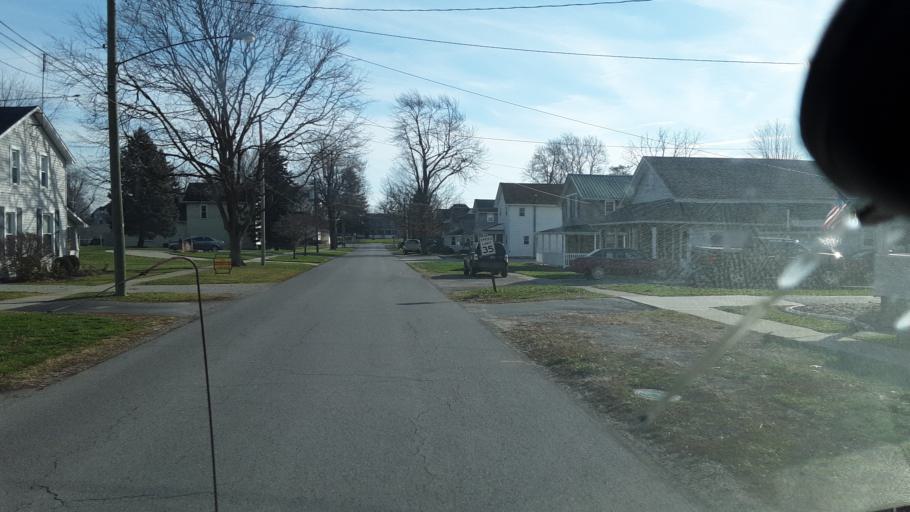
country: US
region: Ohio
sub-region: Defiance County
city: Hicksville
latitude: 41.2914
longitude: -84.7688
